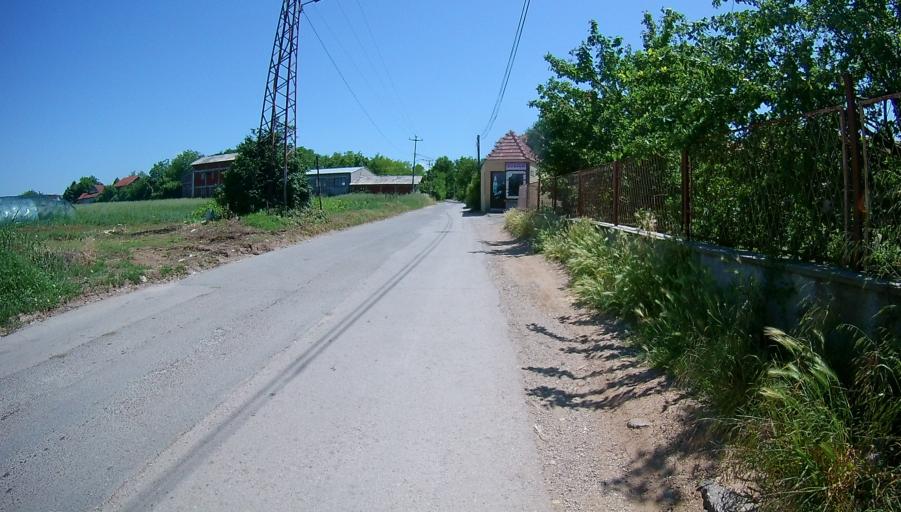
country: RS
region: Central Serbia
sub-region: Nisavski Okrug
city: Nis
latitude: 43.2962
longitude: 21.8977
